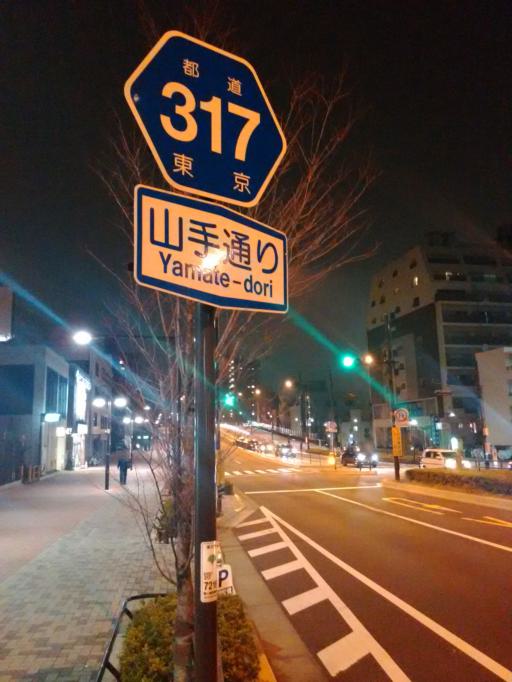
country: JP
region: Tokyo
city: Tokyo
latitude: 35.7131
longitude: 139.6858
